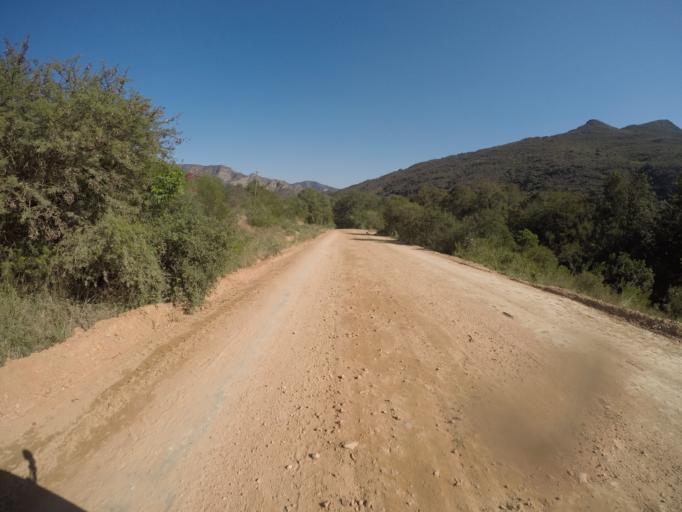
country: ZA
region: Eastern Cape
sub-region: Cacadu District Municipality
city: Kruisfontein
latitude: -33.6631
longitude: 24.5501
